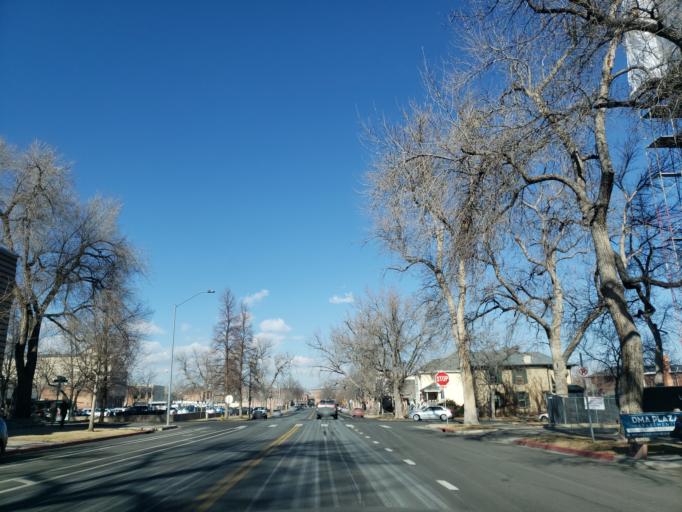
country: US
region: Colorado
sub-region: Larimer County
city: Fort Collins
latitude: 40.5838
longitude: -105.0755
